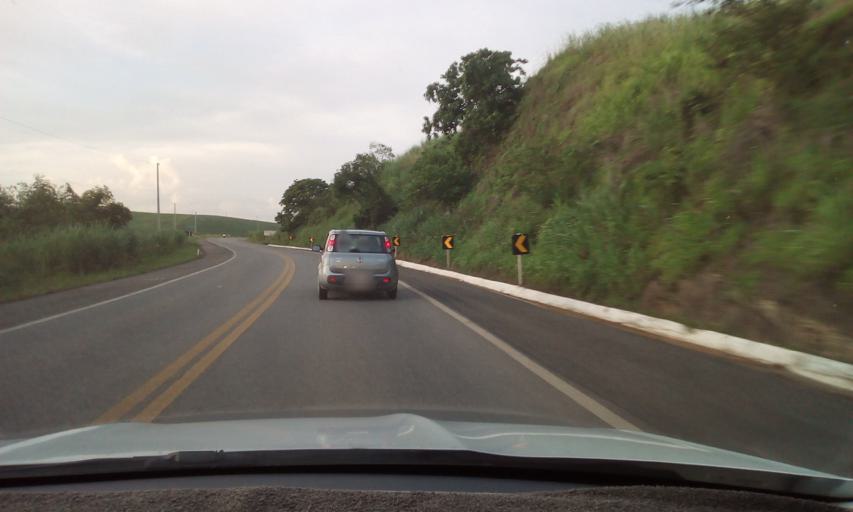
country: BR
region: Pernambuco
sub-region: Vicencia
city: Vicencia
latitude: -7.6226
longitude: -35.2411
